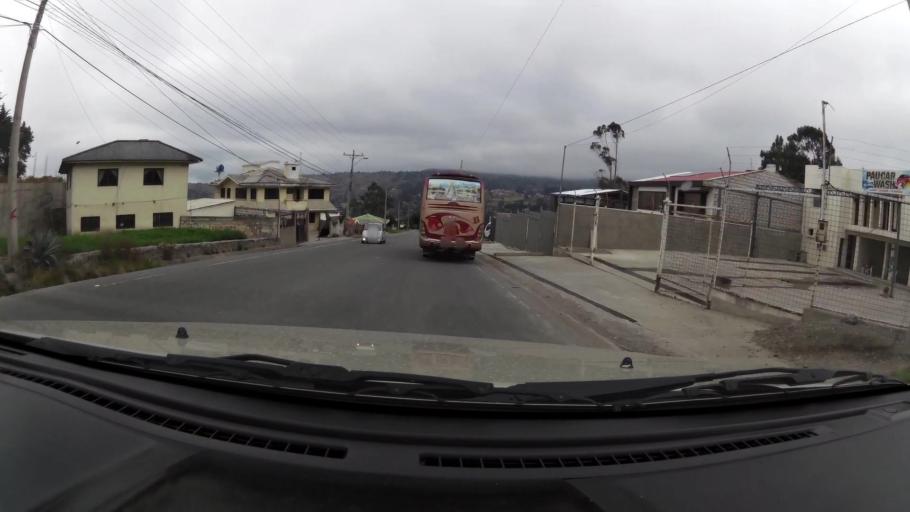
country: EC
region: Canar
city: Canar
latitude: -2.5351
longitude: -78.9322
